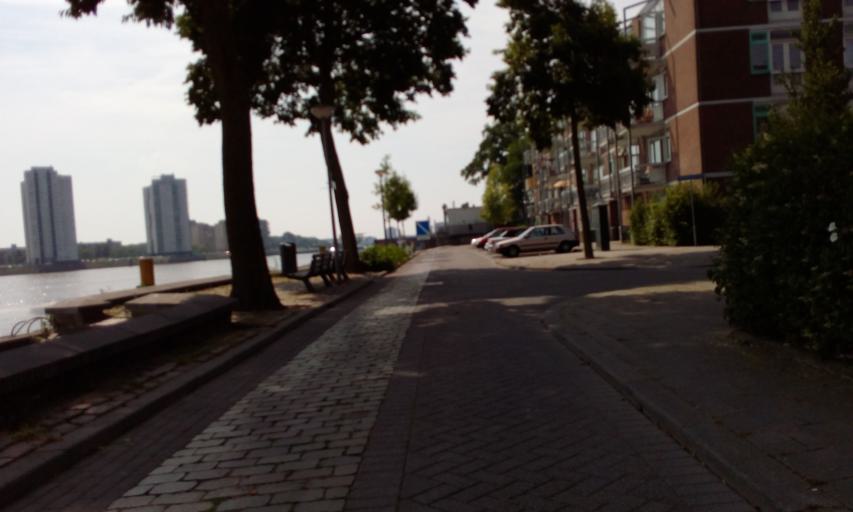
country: NL
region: South Holland
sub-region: Gemeente Rotterdam
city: Rotterdam
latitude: 51.9117
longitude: 4.5128
